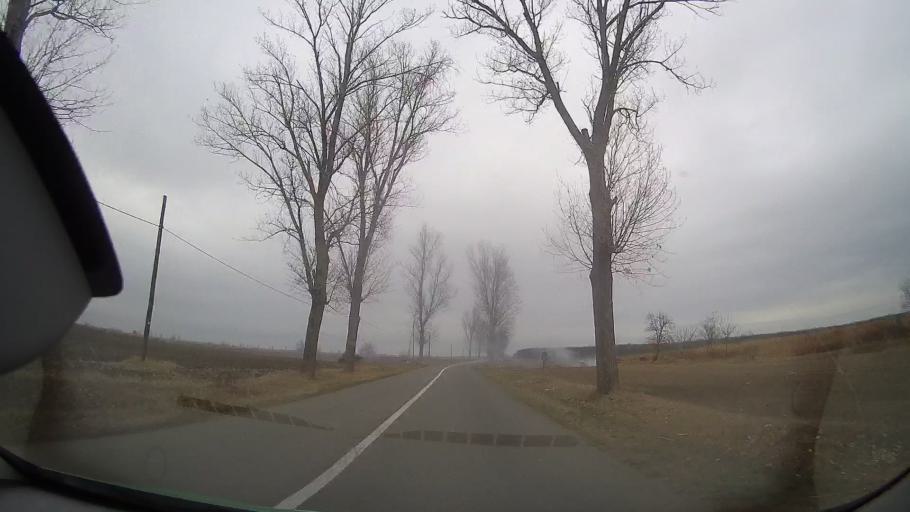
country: RO
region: Braila
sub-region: Comuna Rosiori
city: Rosiori
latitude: 44.8172
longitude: 27.3939
